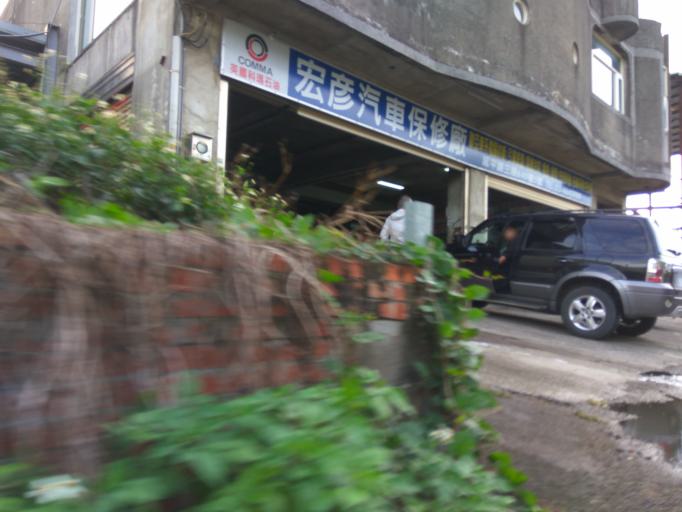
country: TW
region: Taiwan
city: Daxi
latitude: 24.9307
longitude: 121.1958
